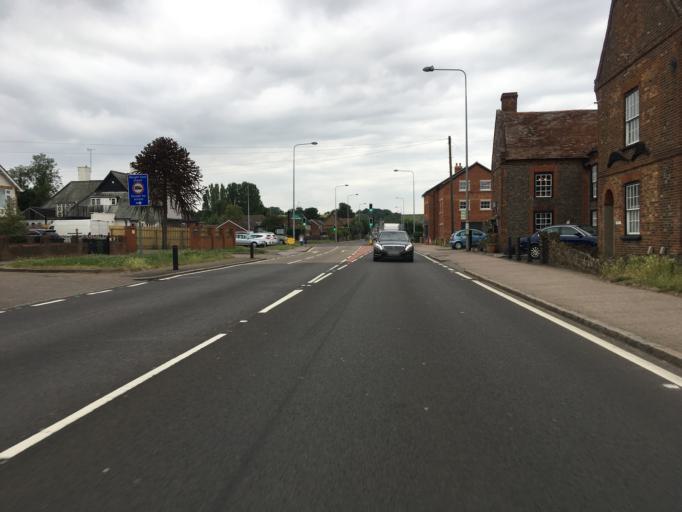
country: GB
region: England
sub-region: Central Bedfordshire
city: Hockliffe
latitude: 51.9303
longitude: -0.5852
